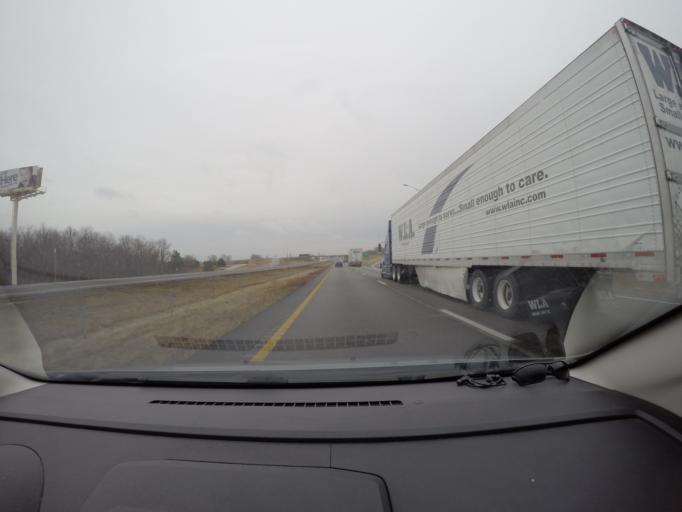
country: US
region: Missouri
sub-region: Warren County
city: Warrenton
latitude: 38.8593
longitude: -91.3080
